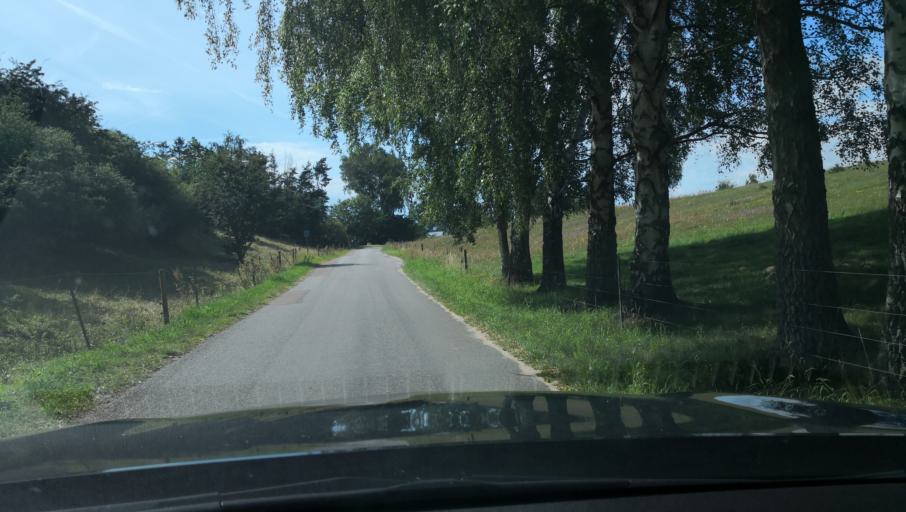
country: SE
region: Skane
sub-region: Ystads Kommun
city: Kopingebro
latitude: 55.3876
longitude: 14.1452
